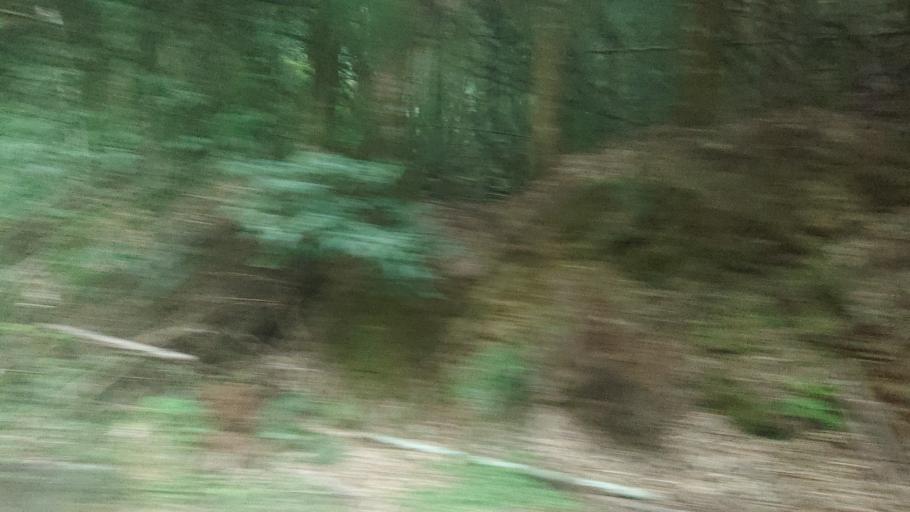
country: TW
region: Taiwan
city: Lugu
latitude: 23.6227
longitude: 120.7189
